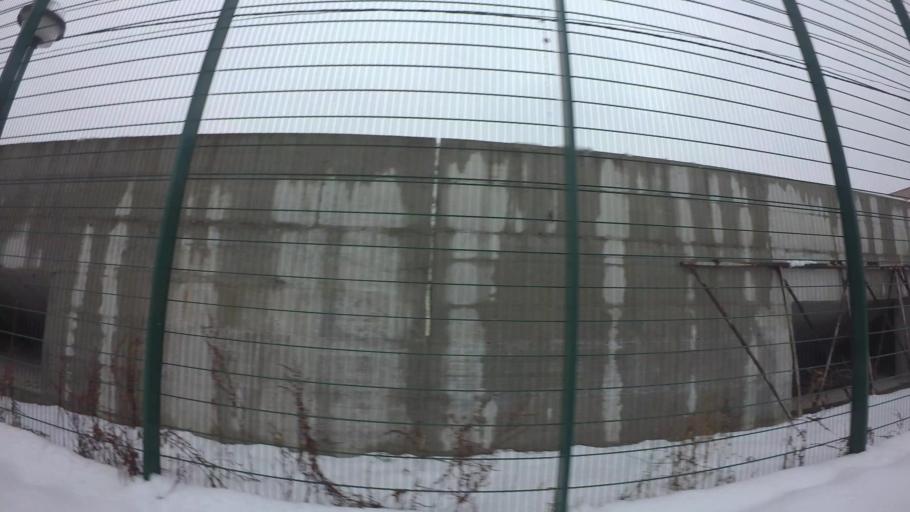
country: BA
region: Federation of Bosnia and Herzegovina
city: Hadzici
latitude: 43.8417
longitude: 18.2787
